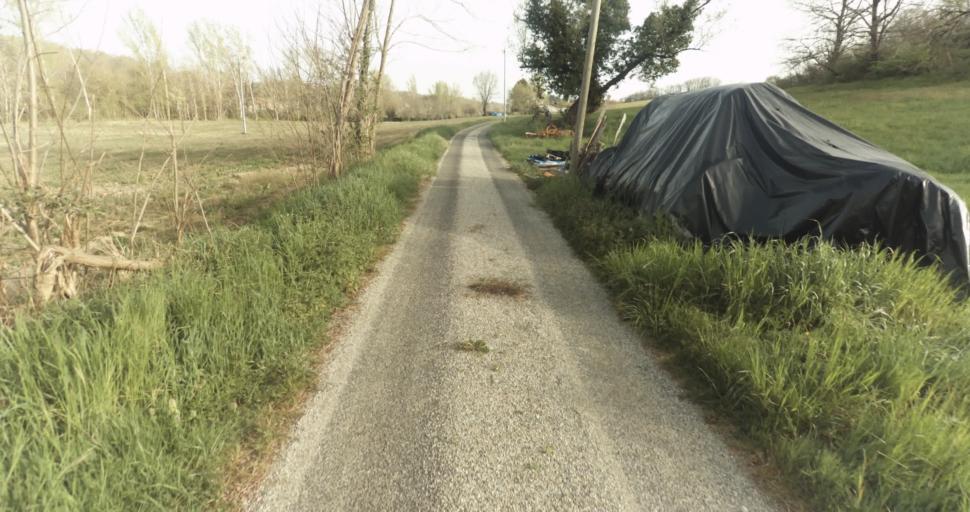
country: FR
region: Midi-Pyrenees
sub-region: Departement du Tarn-et-Garonne
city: Moissac
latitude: 44.1351
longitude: 1.1057
